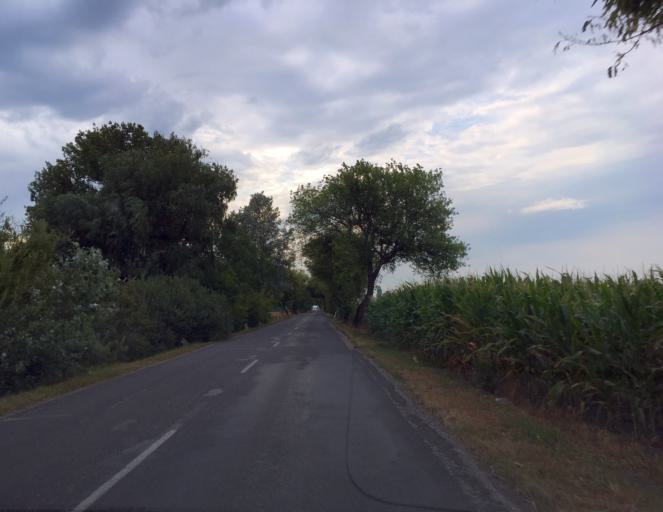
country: SK
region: Trnavsky
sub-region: Okres Dunajska Streda
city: Velky Meder
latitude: 47.9049
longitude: 17.7816
